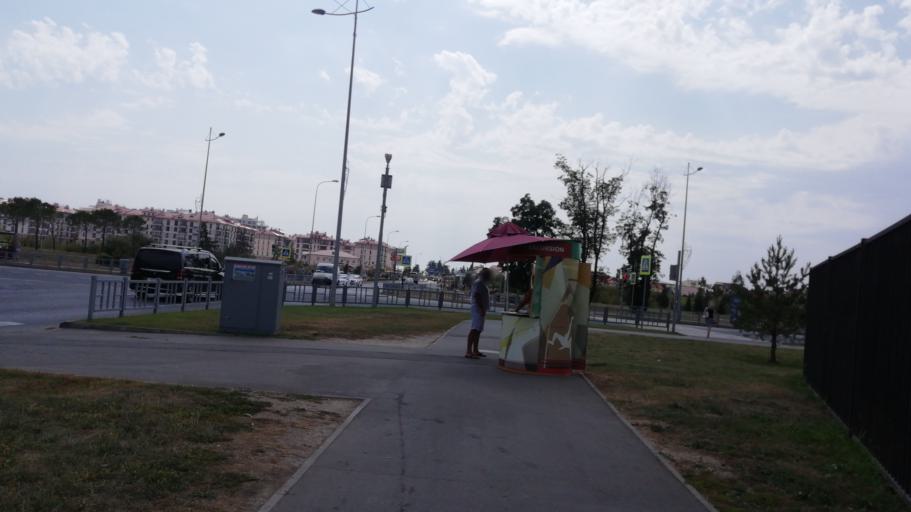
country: RU
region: Krasnodarskiy
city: Adler
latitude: 43.4009
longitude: 39.9772
